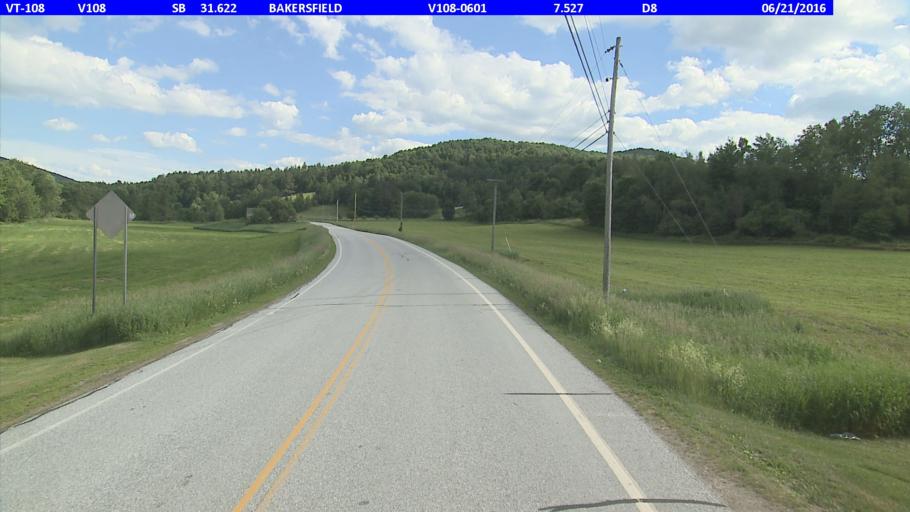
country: US
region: Vermont
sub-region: Franklin County
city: Enosburg Falls
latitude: 44.8314
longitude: -72.8032
